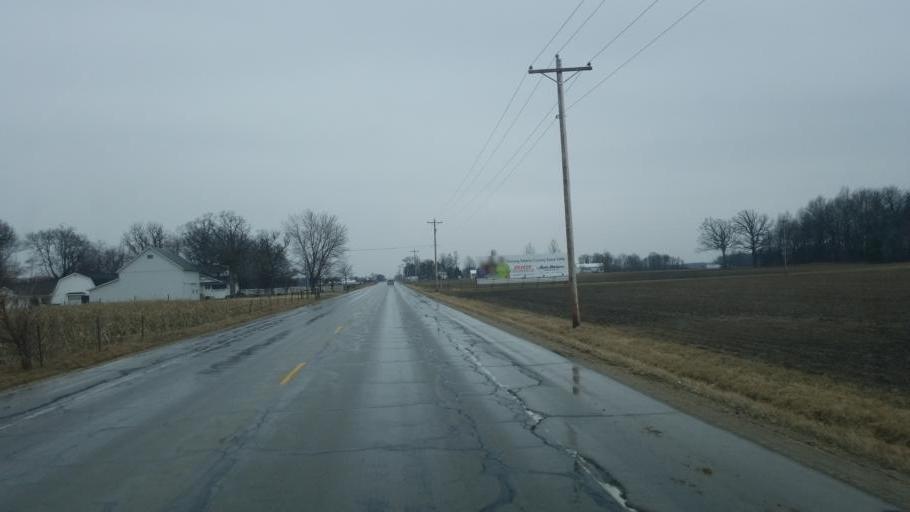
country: US
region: Indiana
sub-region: Adams County
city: Berne
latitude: 40.6988
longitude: -84.9559
